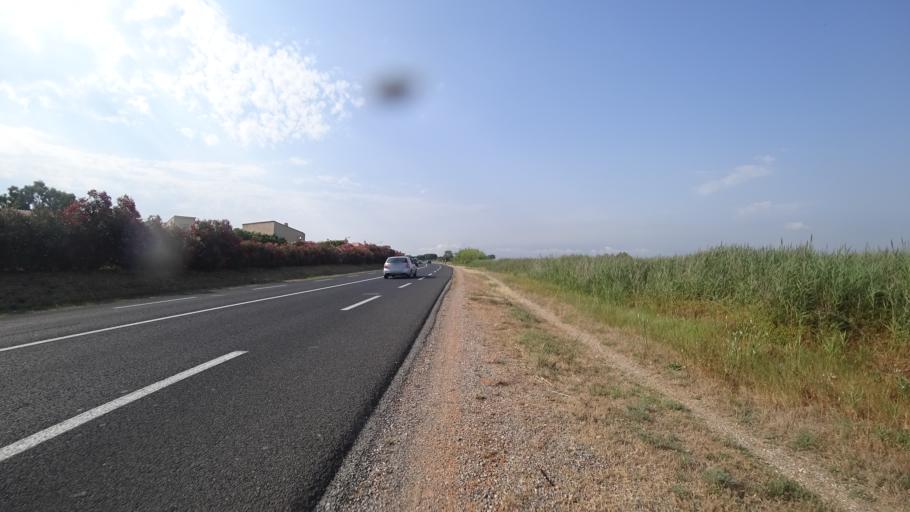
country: FR
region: Languedoc-Roussillon
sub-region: Departement des Pyrenees-Orientales
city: Canet-en-Roussillon
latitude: 42.6817
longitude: 3.0282
